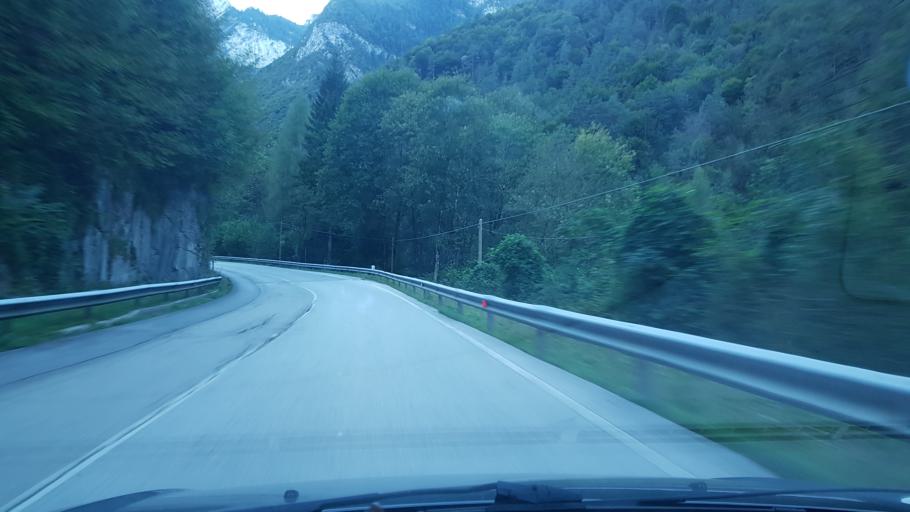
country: IT
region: Veneto
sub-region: Provincia di Belluno
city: Forno di Zoldo
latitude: 46.3155
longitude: 12.2287
